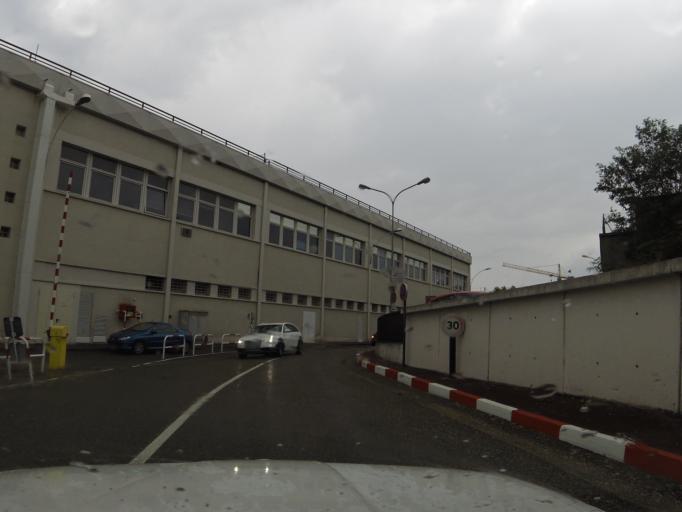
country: FR
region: Rhone-Alpes
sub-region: Departement du Rhone
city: Bron
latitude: 45.7318
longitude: 4.8900
